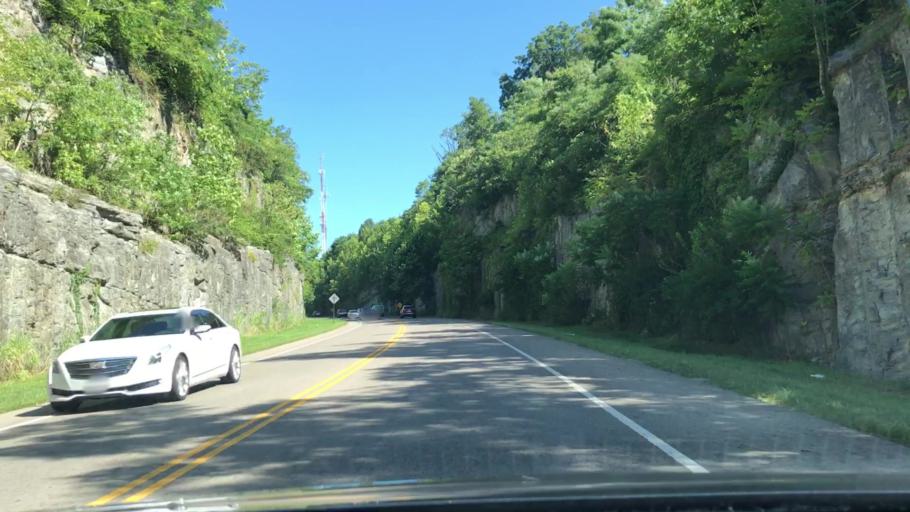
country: US
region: Tennessee
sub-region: Williamson County
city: Franklin
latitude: 35.9778
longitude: -86.8407
